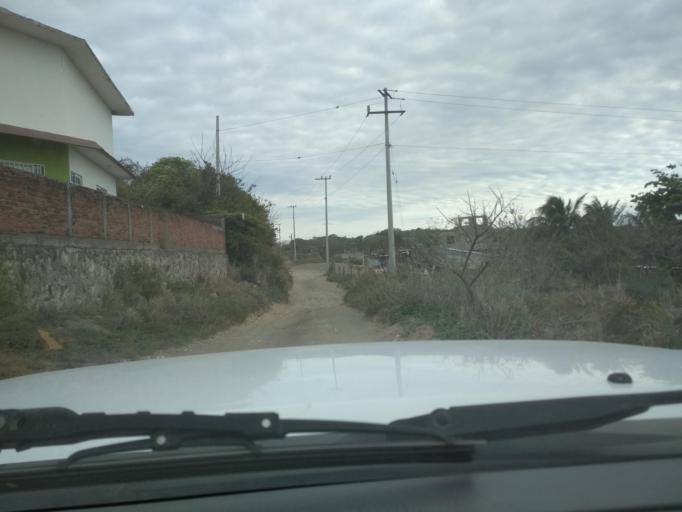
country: MX
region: Veracruz
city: Anton Lizardo
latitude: 19.0540
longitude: -95.9930
